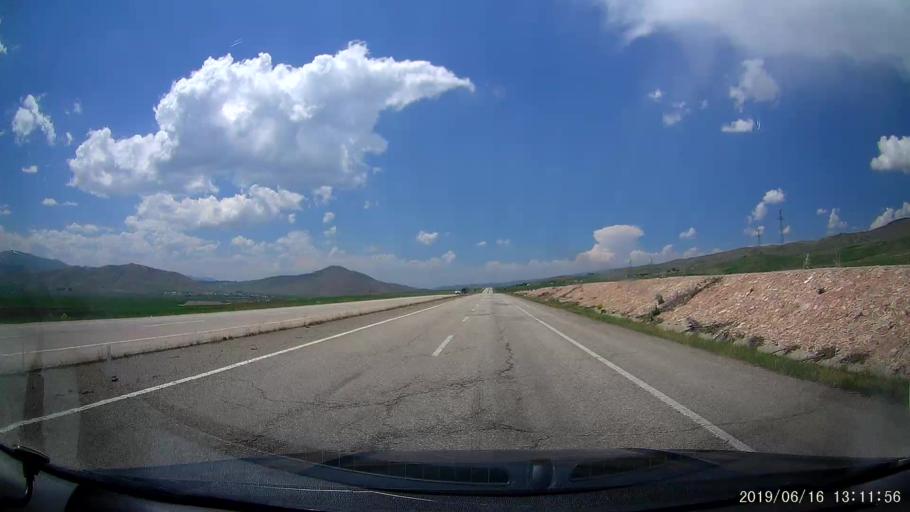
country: TR
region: Agri
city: Diyadin
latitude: 39.5953
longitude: 43.5935
